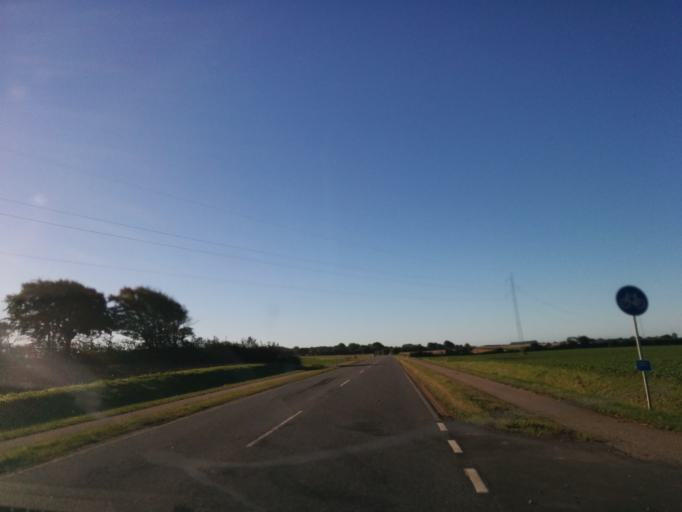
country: DK
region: South Denmark
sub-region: Kolding Kommune
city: Sonder Bjert
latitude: 55.4451
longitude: 9.5563
